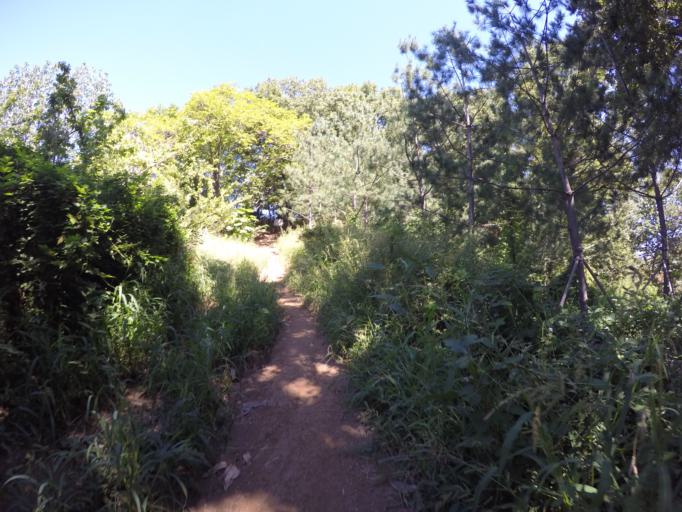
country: KR
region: Seoul
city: Seoul
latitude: 37.4864
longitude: 127.0417
